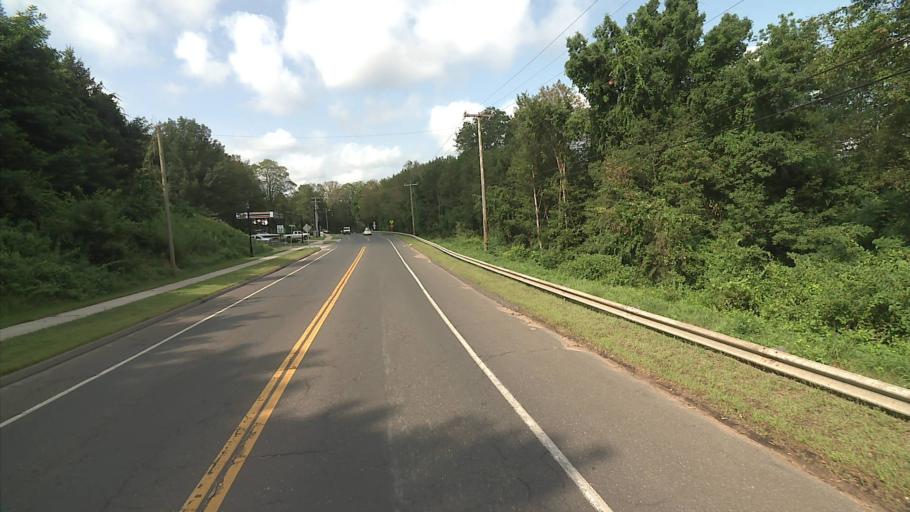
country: US
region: Connecticut
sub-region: Middlesex County
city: Moodus
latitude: 41.5038
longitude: -72.4488
